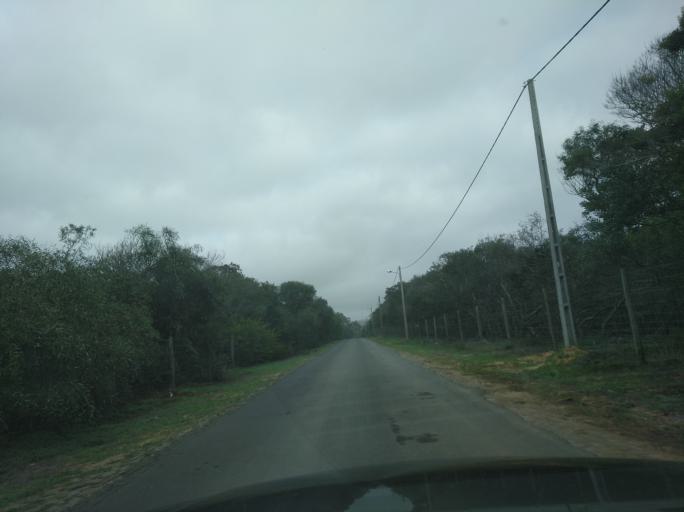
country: PT
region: Setubal
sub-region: Sines
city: Porto Covo
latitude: 37.8290
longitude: -8.7894
